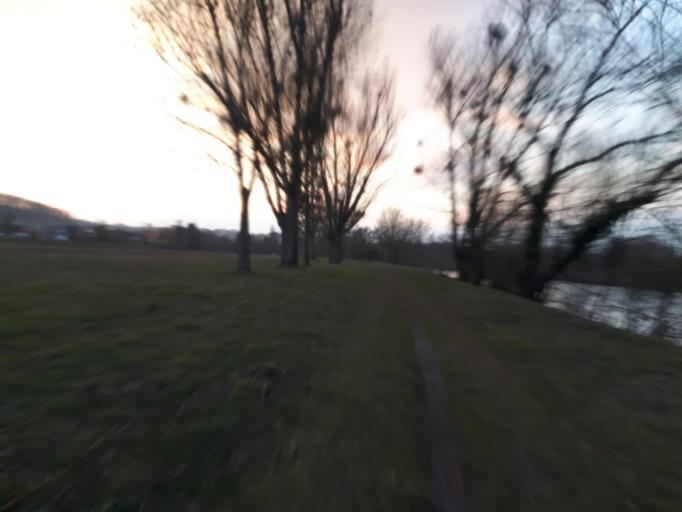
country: DE
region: Baden-Wuerttemberg
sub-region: Regierungsbezirk Stuttgart
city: Untereisesheim
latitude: 49.2325
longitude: 9.1888
